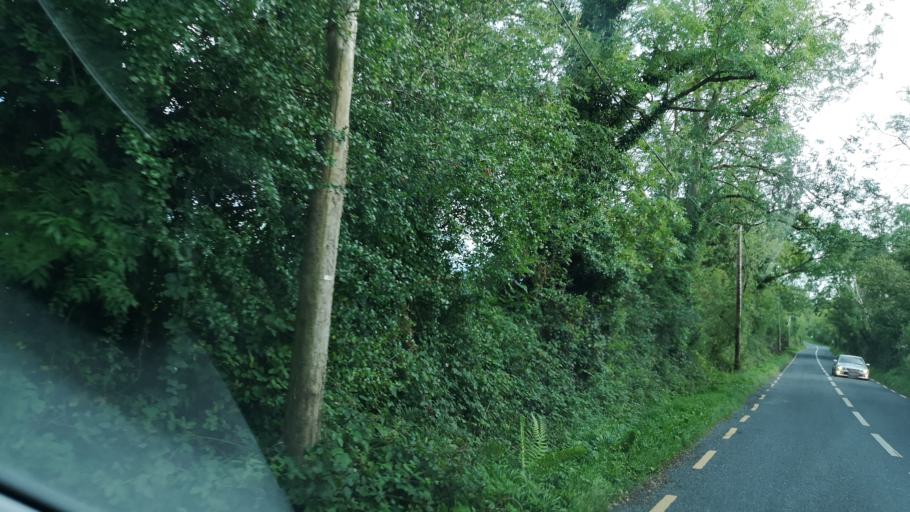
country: IE
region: Connaught
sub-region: County Galway
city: Ballinasloe
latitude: 53.3158
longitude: -8.2799
